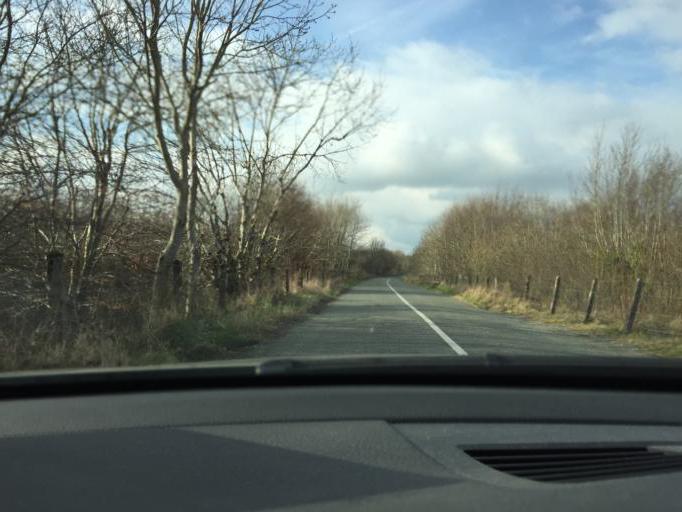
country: IE
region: Leinster
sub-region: Wicklow
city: Valleymount
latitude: 53.1110
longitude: -6.5276
